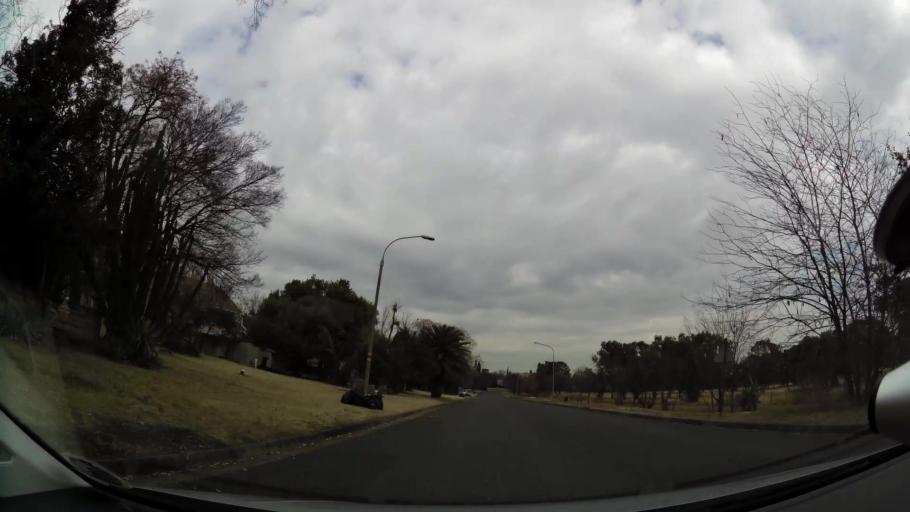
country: ZA
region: Orange Free State
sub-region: Fezile Dabi District Municipality
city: Kroonstad
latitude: -27.6704
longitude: 27.2457
